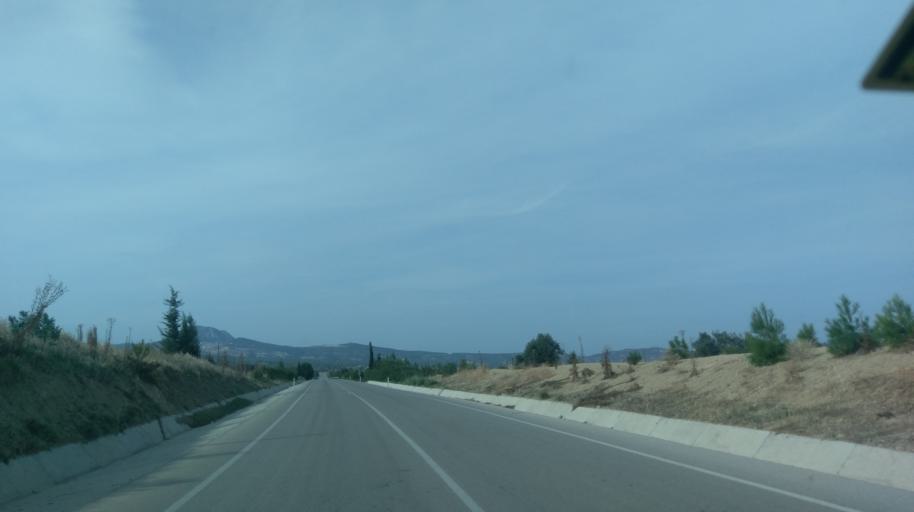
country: CY
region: Ammochostos
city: Leonarisso
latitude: 35.3916
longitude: 34.0084
